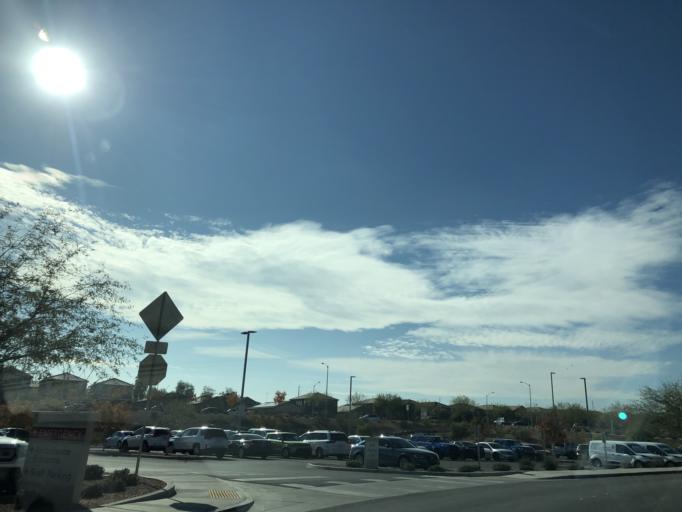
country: US
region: Nevada
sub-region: Clark County
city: Whitney
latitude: 36.0721
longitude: -115.0296
